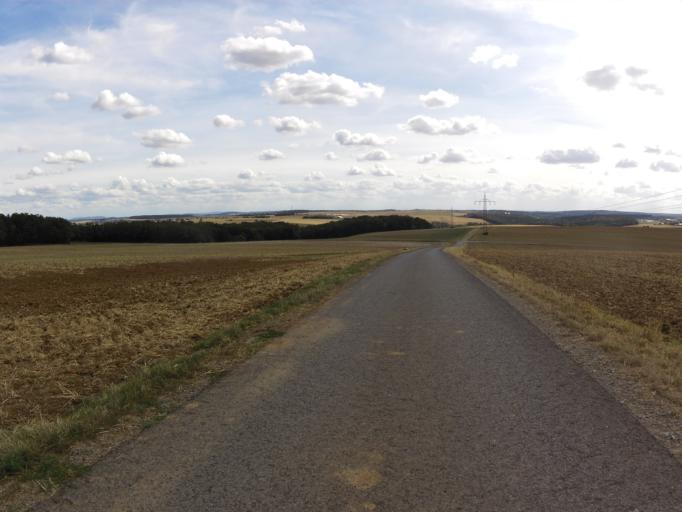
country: DE
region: Bavaria
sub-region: Regierungsbezirk Unterfranken
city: Guntersleben
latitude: 49.8677
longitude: 9.9148
